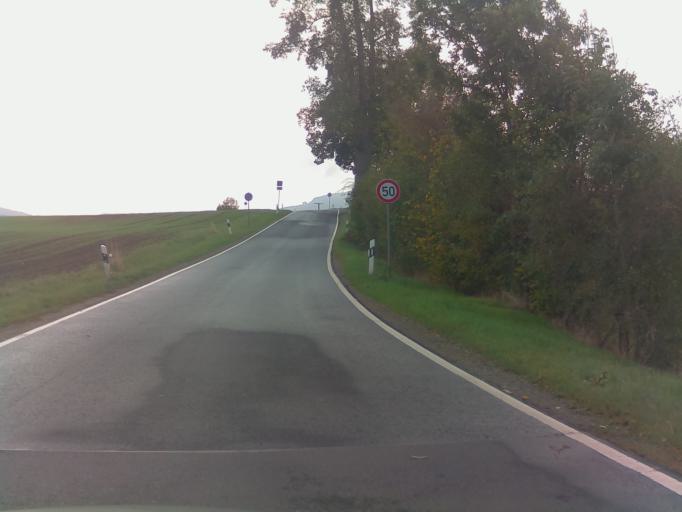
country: DE
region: Hesse
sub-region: Regierungsbezirk Kassel
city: Hofbieber
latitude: 50.5775
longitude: 9.8120
